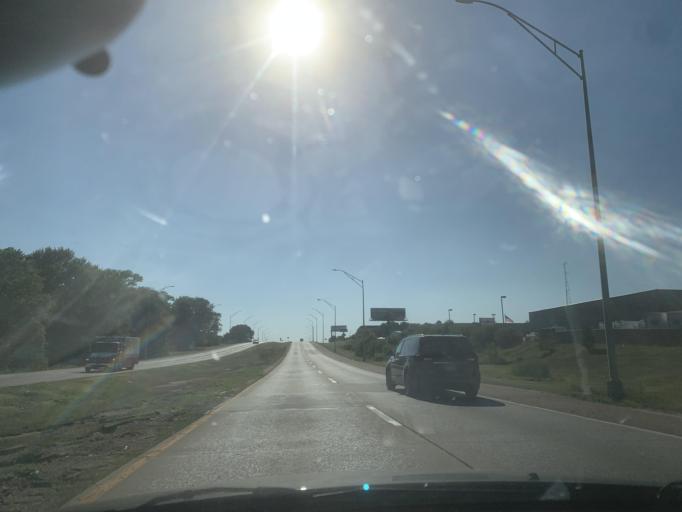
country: US
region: Nebraska
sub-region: Douglas County
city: Ralston
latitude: 41.2126
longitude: -96.0744
